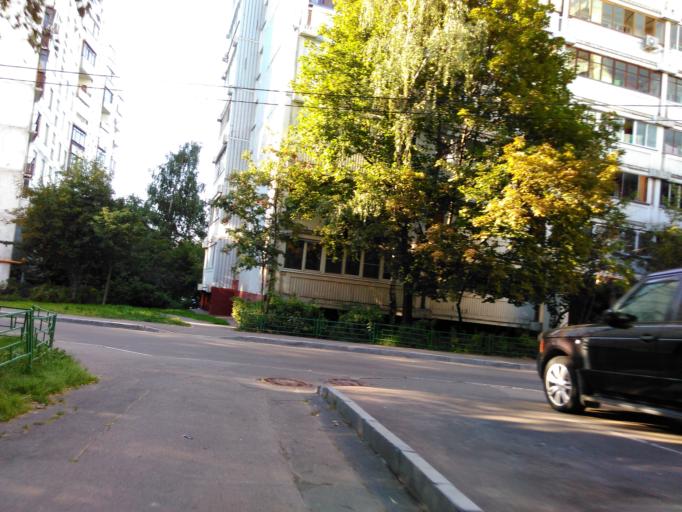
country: RU
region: Moscow
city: Tyoply Stan
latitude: 55.6307
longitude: 37.5094
